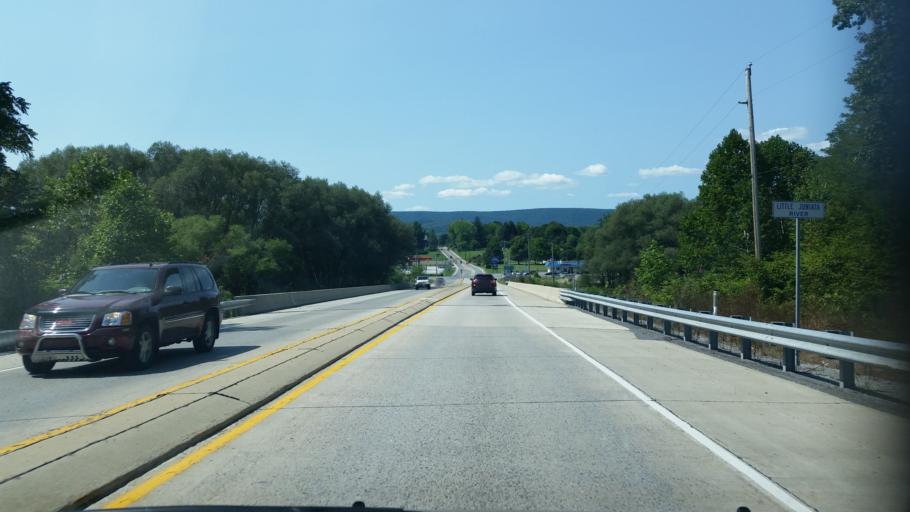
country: US
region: Pennsylvania
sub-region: Blair County
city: Bellwood
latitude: 40.5994
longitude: -78.3171
